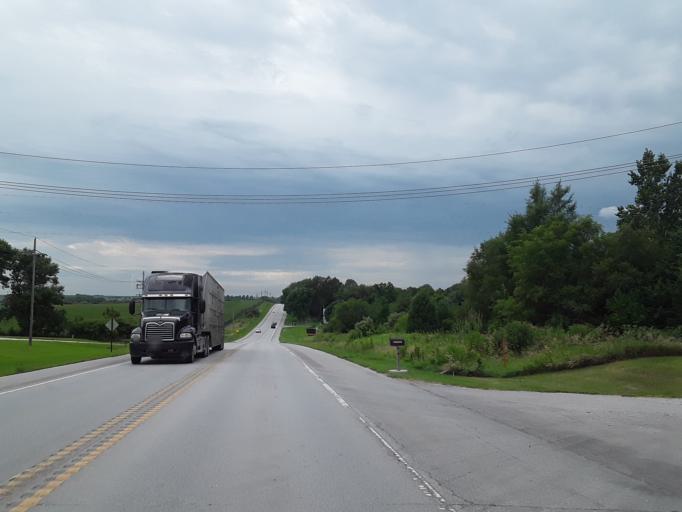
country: US
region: Nebraska
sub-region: Saunders County
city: Yutan
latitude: 41.2339
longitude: -96.3762
